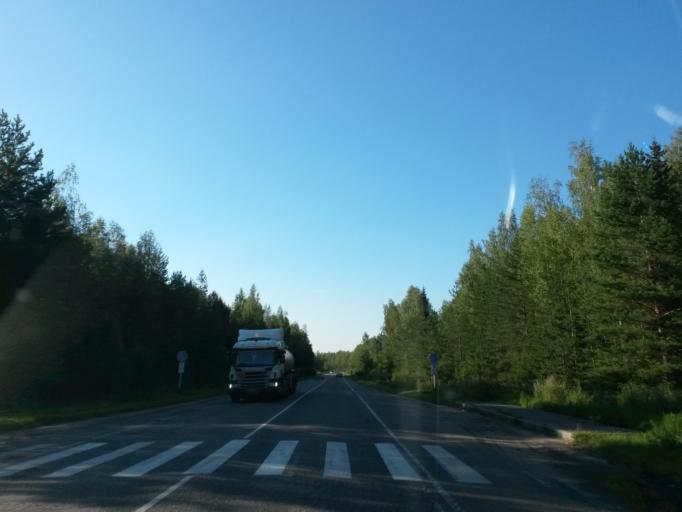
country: RU
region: Ivanovo
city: Pistsovo
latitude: 57.0827
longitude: 40.6731
